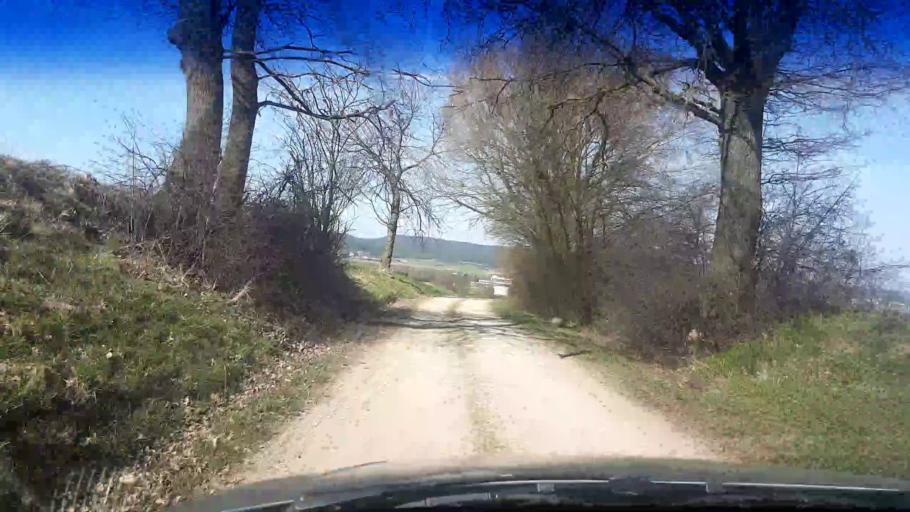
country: DE
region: Bavaria
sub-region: Upper Franconia
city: Bischberg
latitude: 49.9022
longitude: 10.8249
